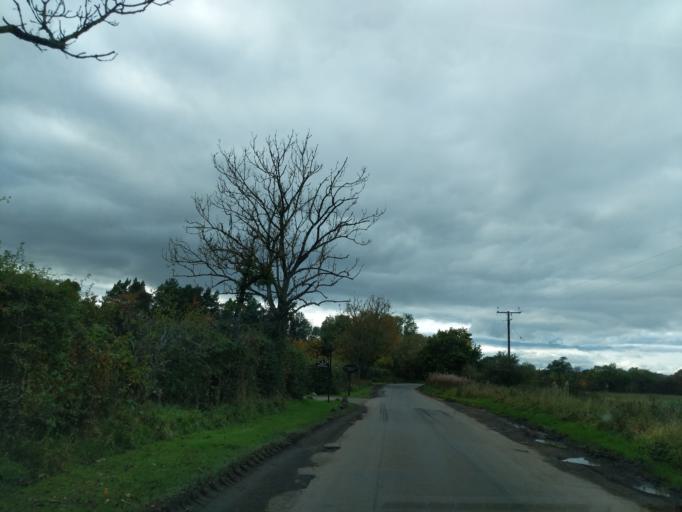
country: GB
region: Scotland
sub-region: East Lothian
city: Macmerry
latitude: 55.9417
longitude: -2.8459
